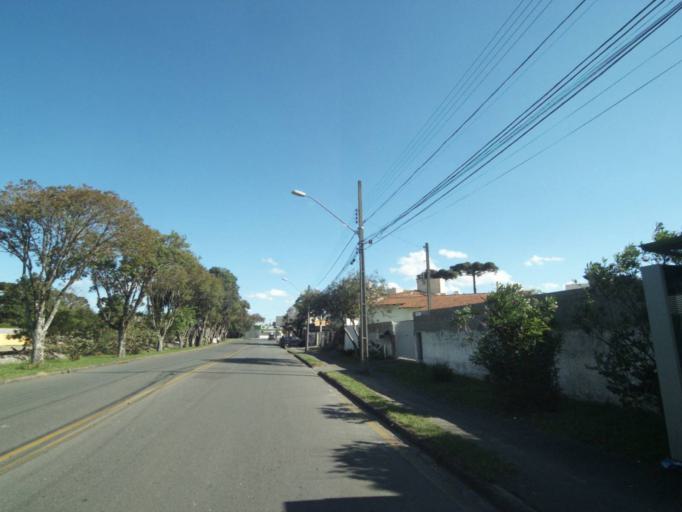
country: BR
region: Parana
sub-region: Curitiba
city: Curitiba
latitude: -25.3926
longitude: -49.2582
